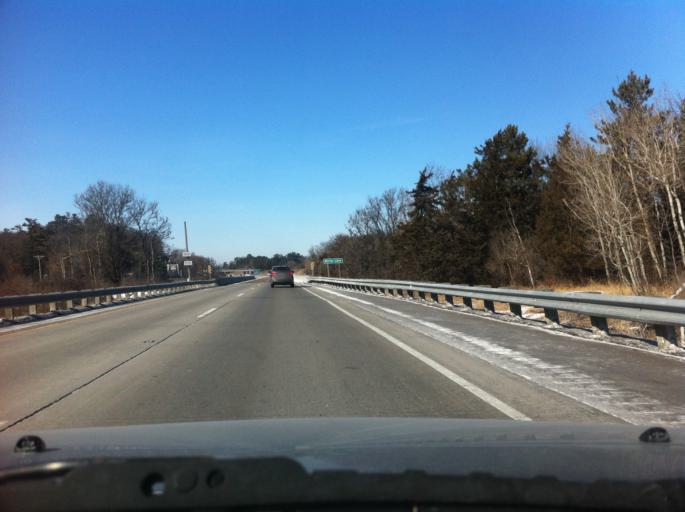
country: US
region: Wisconsin
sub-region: Sauk County
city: Lake Delton
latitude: 43.5657
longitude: -89.7448
